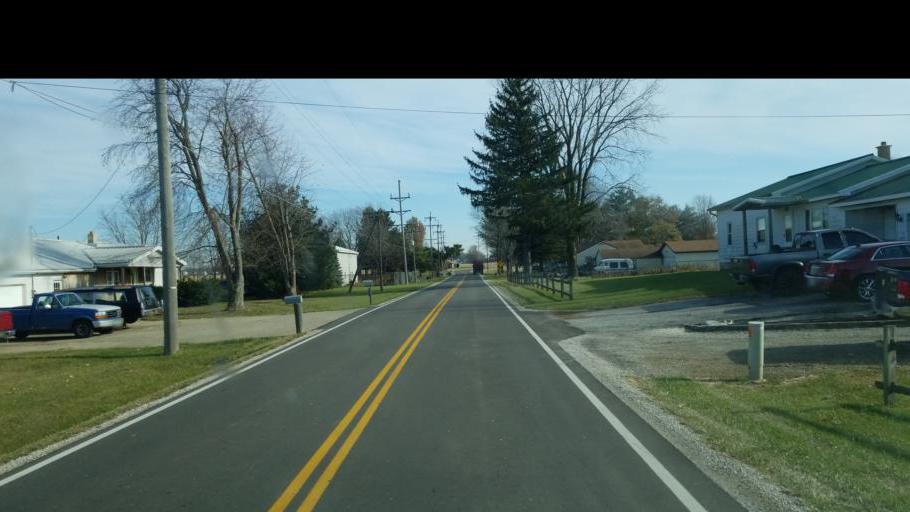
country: US
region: Ohio
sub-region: Crawford County
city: Galion
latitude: 40.7846
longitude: -82.8728
